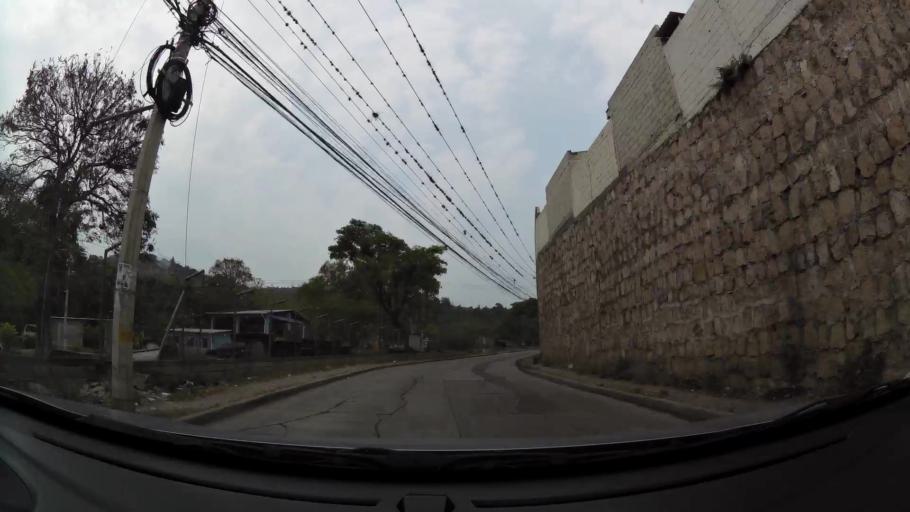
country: HN
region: Francisco Morazan
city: Tegucigalpa
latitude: 14.0704
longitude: -87.2357
